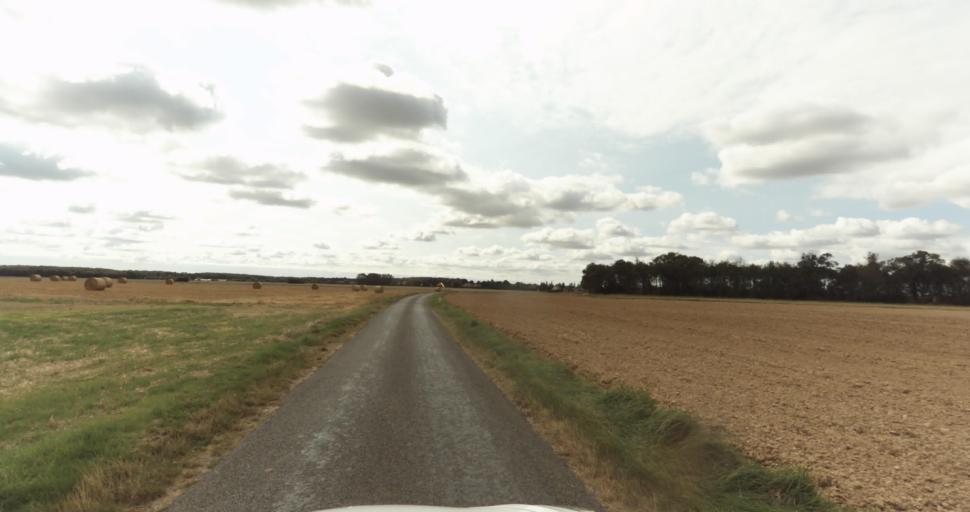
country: FR
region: Haute-Normandie
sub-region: Departement de l'Eure
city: Tillieres-sur-Avre
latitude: 48.7877
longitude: 1.1012
